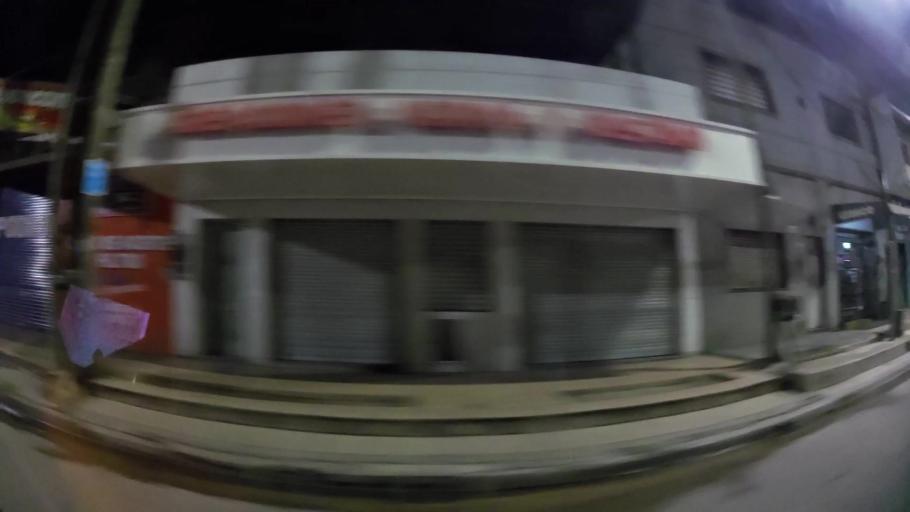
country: AR
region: Buenos Aires
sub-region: Partido de Lanus
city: Lanus
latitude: -34.7192
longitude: -58.3592
